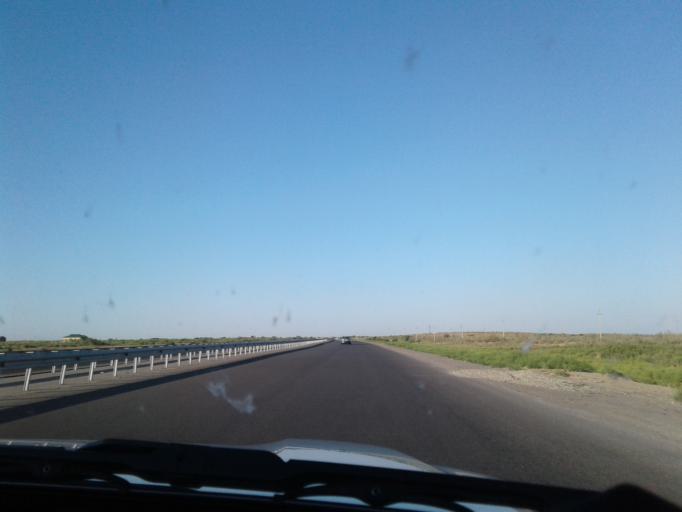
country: TM
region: Mary
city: Mary
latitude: 37.4311
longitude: 61.6121
